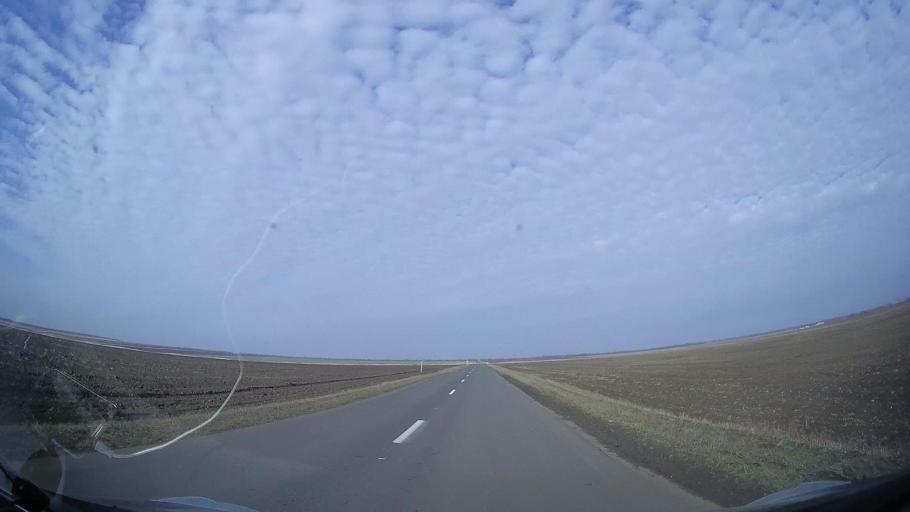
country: RU
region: Rostov
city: Gigant
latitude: 46.8778
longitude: 41.2712
